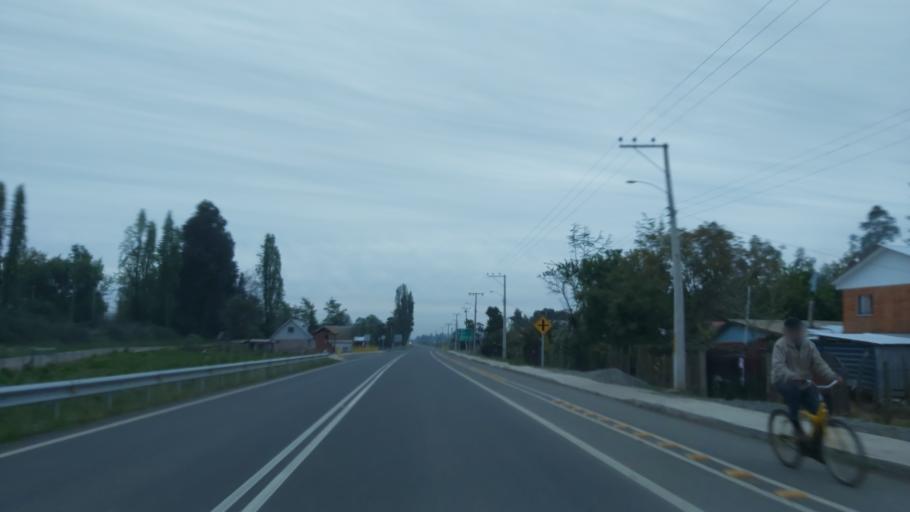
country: CL
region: Maule
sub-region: Provincia de Linares
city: Colbun
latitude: -35.6750
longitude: -71.4671
